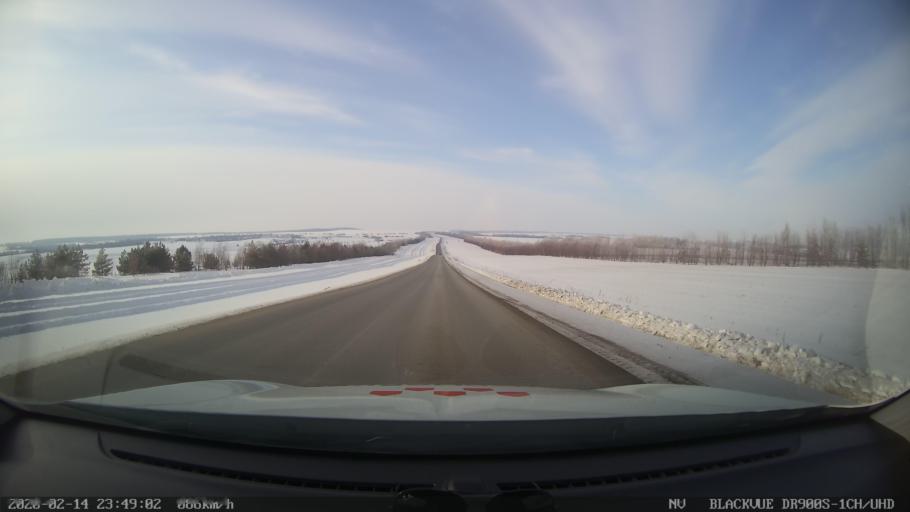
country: RU
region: Tatarstan
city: Kuybyshevskiy Zaton
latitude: 55.2510
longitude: 49.1911
